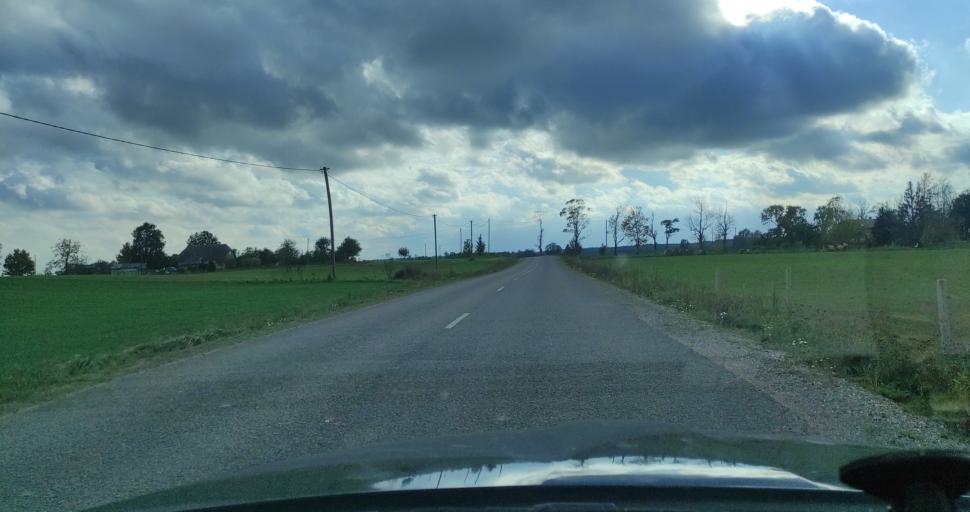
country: LV
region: Talsu Rajons
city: Sabile
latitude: 56.9433
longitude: 22.3976
